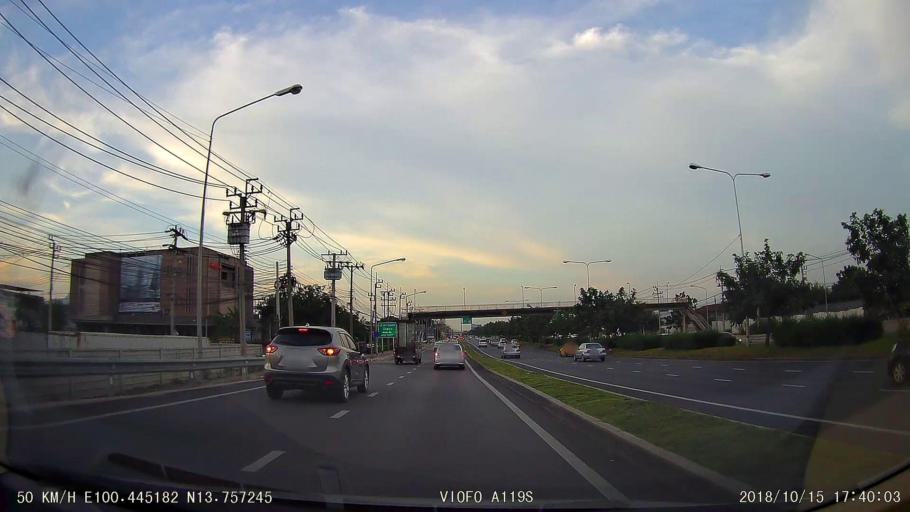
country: TH
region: Bangkok
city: Taling Chan
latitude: 13.7575
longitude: 100.4451
